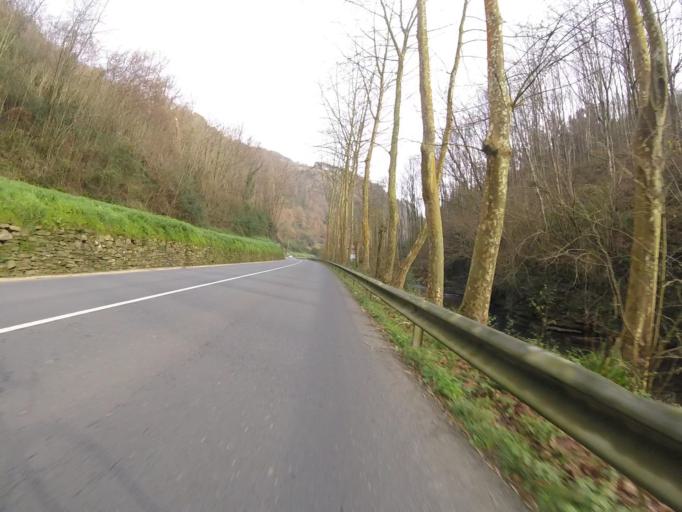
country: ES
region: Basque Country
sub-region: Provincia de Guipuzcoa
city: Belaunza
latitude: 43.1380
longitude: -2.0563
